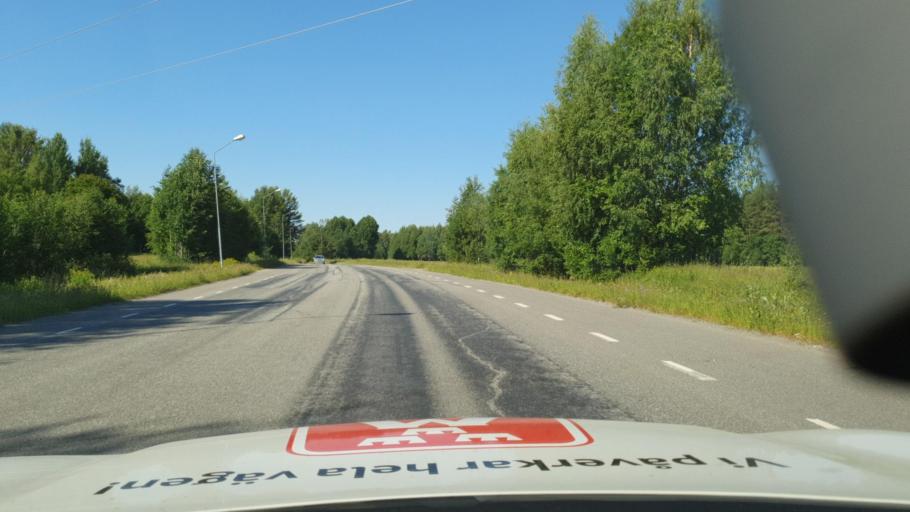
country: SE
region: Vaesterbotten
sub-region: Skelleftea Kommun
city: Viken
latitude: 64.7587
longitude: 20.8733
